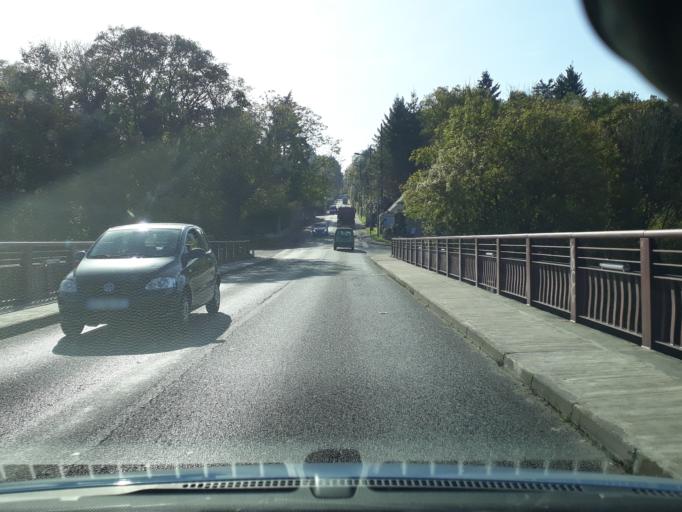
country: FR
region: Ile-de-France
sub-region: Departement de Seine-et-Marne
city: Chartrettes
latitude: 48.4811
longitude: 2.6952
